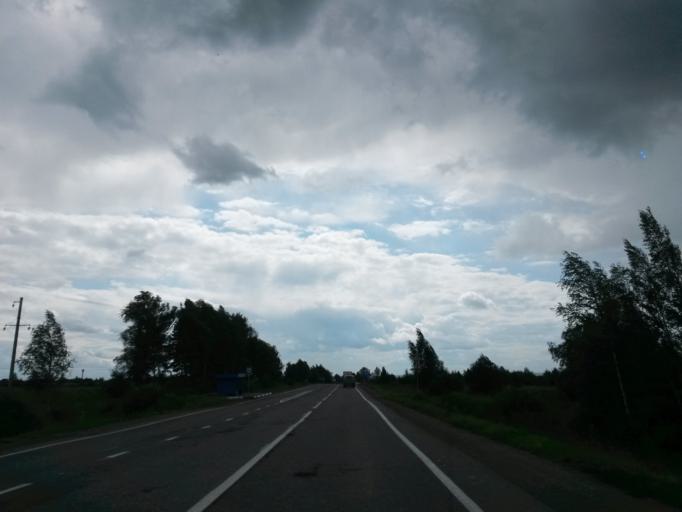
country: RU
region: Jaroslavl
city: Gavrilov-Yam
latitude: 57.3619
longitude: 39.9080
